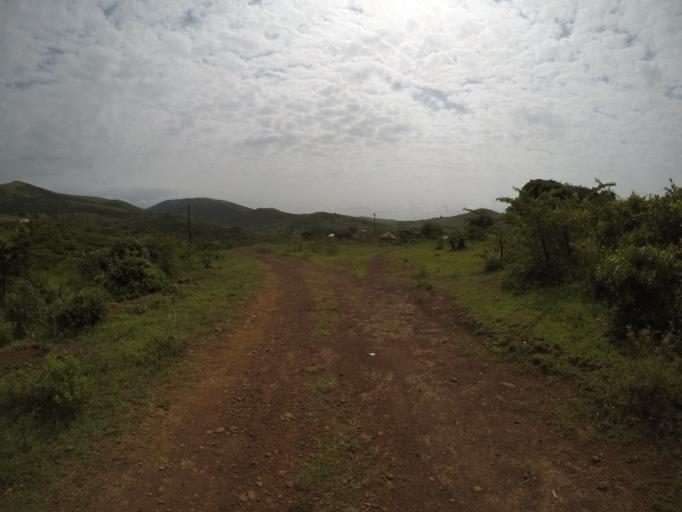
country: ZA
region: KwaZulu-Natal
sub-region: uThungulu District Municipality
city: Empangeni
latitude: -28.6224
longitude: 31.9090
